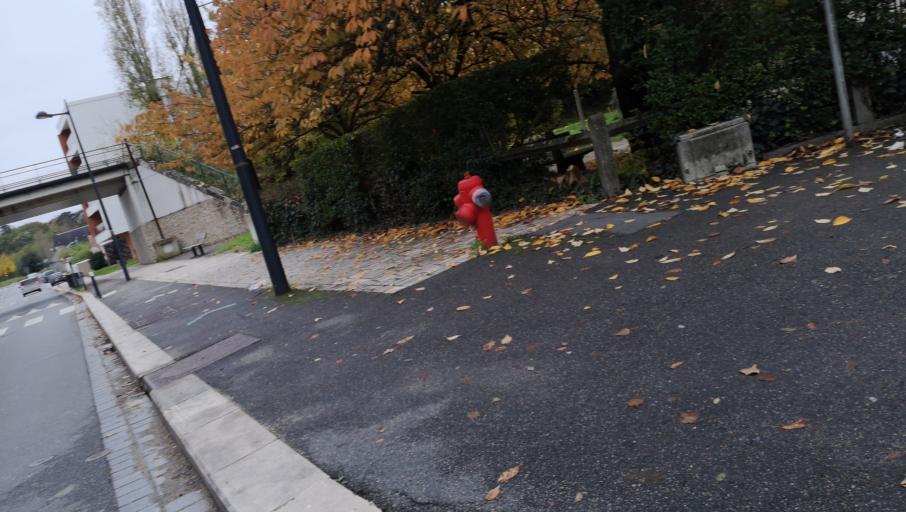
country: FR
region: Centre
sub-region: Departement du Loiret
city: Saint-Jean-de-Braye
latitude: 47.9101
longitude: 1.9711
